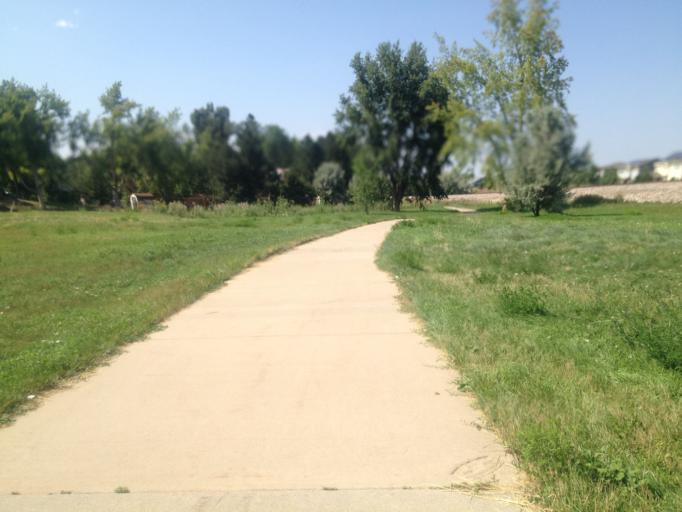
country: US
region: Colorado
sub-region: Boulder County
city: Louisville
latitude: 39.9913
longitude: -105.1357
